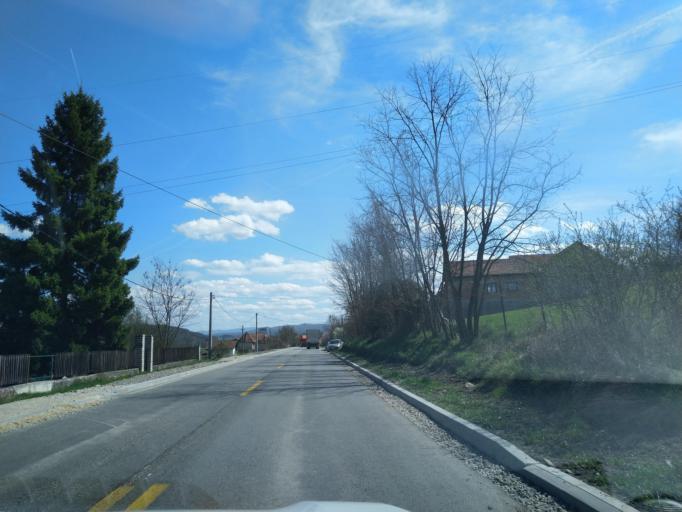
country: RS
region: Central Serbia
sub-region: Zlatiborski Okrug
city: Pozega
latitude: 43.8299
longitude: 20.0750
